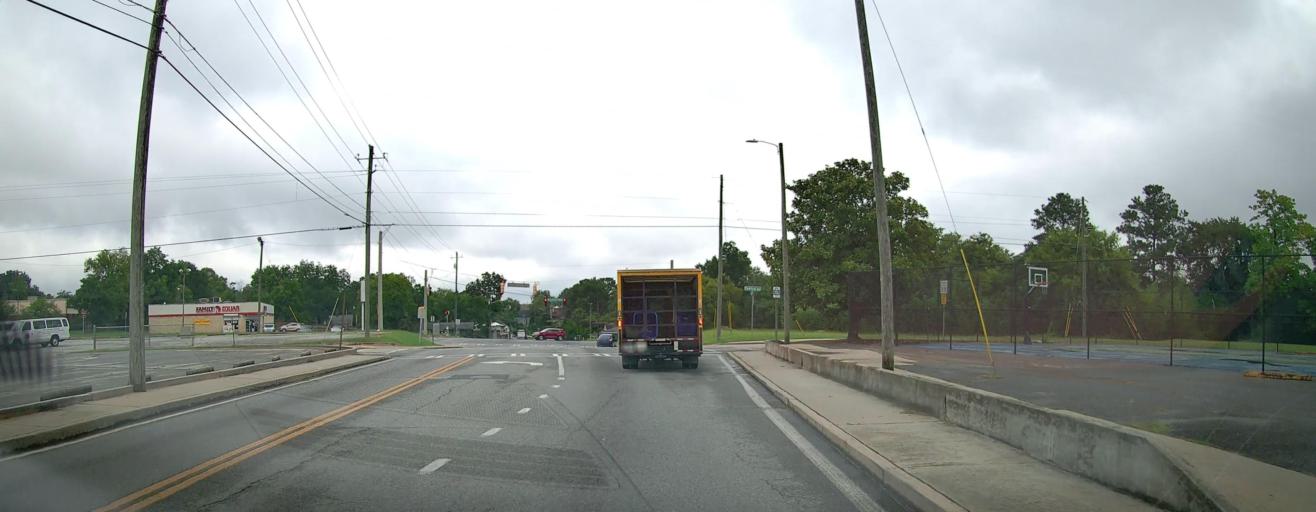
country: US
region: Georgia
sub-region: Bibb County
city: Macon
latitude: 32.8130
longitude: -83.6451
